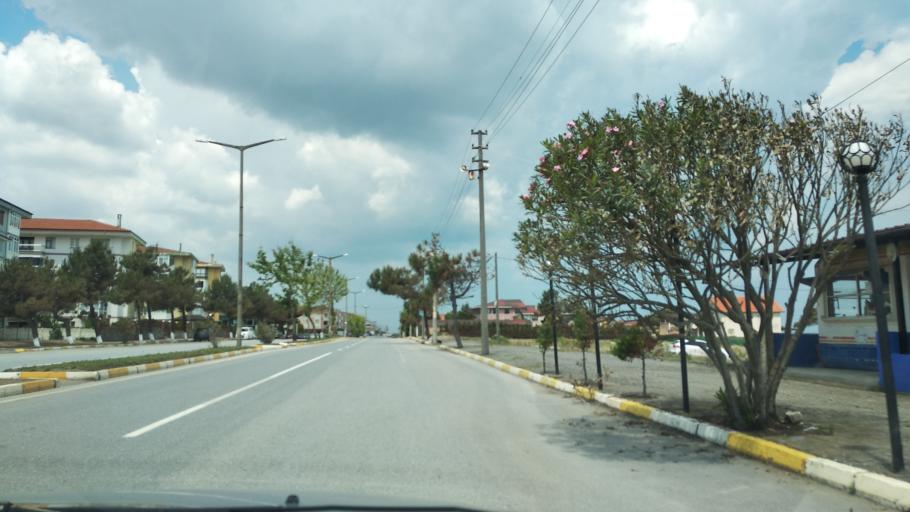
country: TR
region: Sakarya
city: Karasu
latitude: 41.1125
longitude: 30.6861
